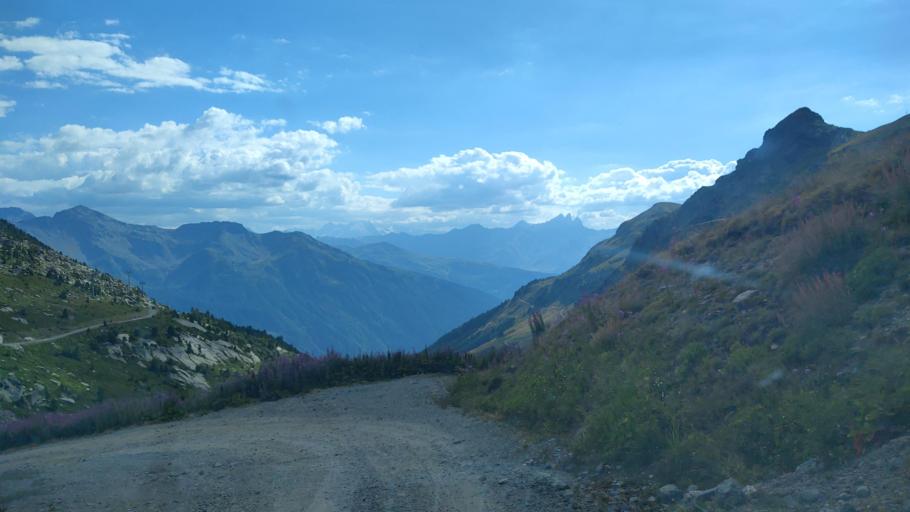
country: FR
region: Rhone-Alpes
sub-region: Departement de la Savoie
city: Val Thorens
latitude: 45.2451
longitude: 6.5684
